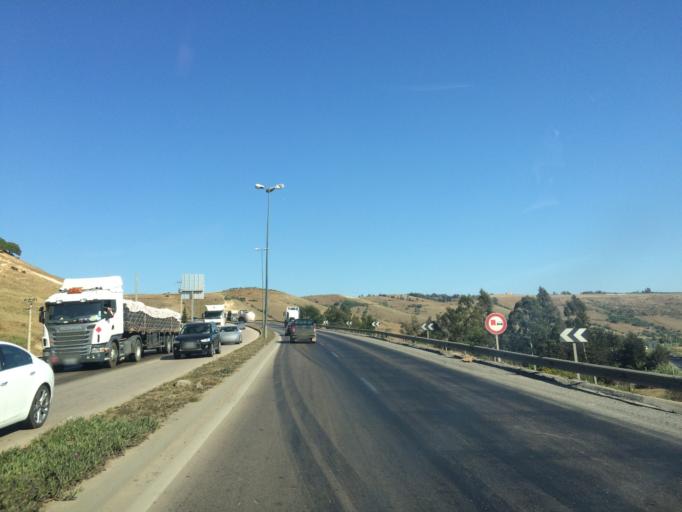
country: MA
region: Rabat-Sale-Zemmour-Zaer
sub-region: Rabat
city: Rabat
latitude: 33.9861
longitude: -6.7614
